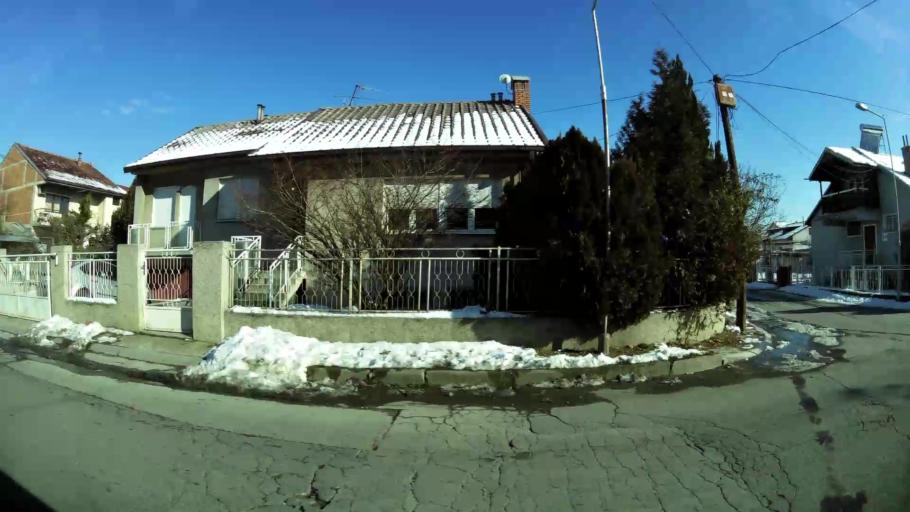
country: MK
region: Saraj
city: Saraj
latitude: 42.0092
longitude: 21.3400
